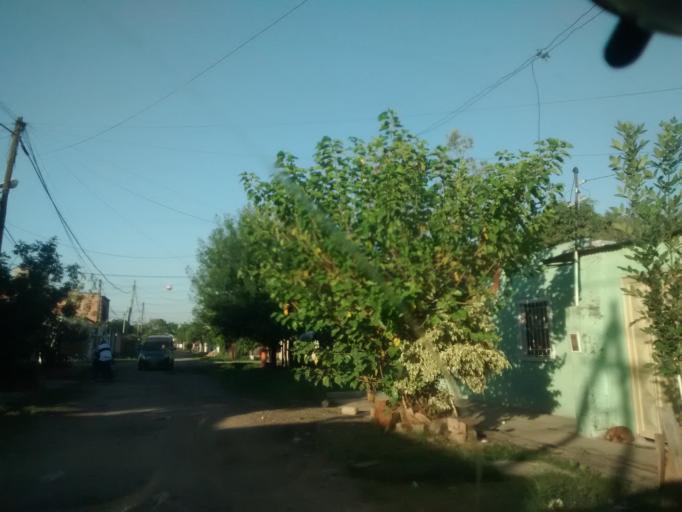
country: AR
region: Chaco
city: Resistencia
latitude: -27.4666
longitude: -58.9804
